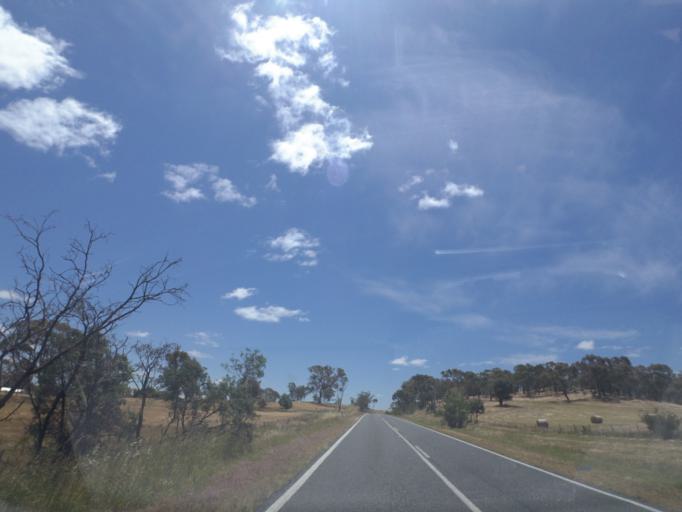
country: AU
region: Victoria
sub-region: Mount Alexander
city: Castlemaine
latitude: -37.2165
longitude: 144.1405
